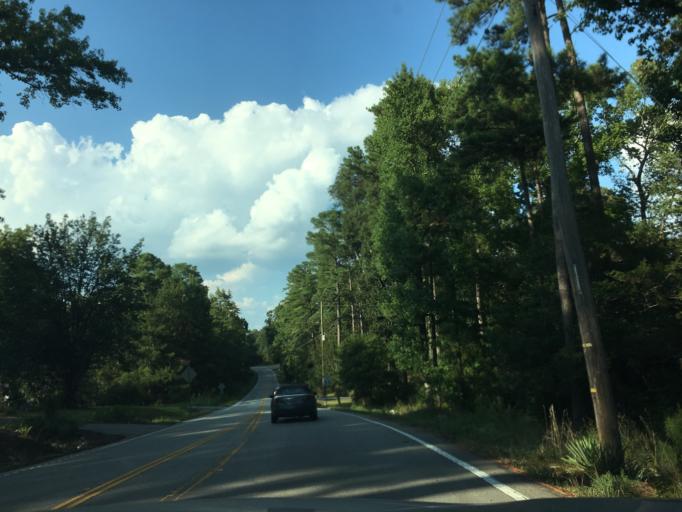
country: US
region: South Carolina
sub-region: Richland County
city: Lake Murray of Richland
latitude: 34.1275
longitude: -81.2166
